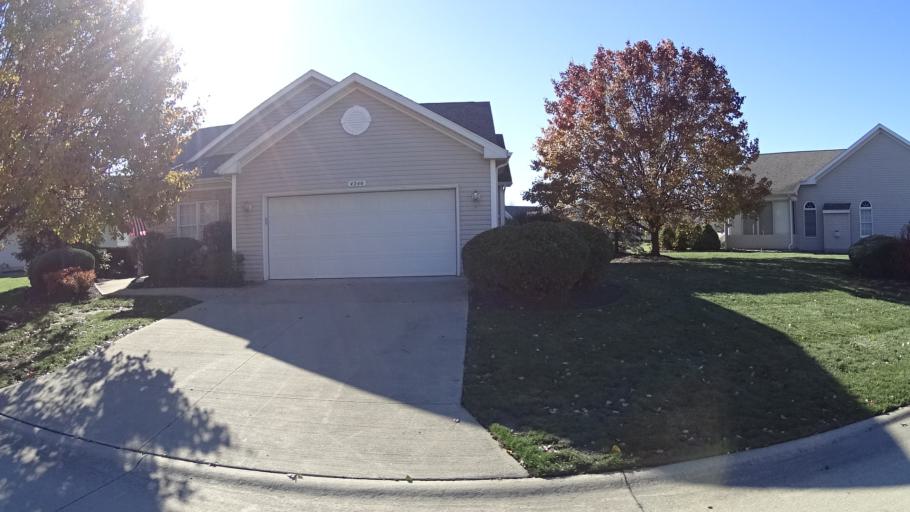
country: US
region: Ohio
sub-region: Lorain County
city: Avon Center
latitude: 41.4343
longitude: -81.9998
